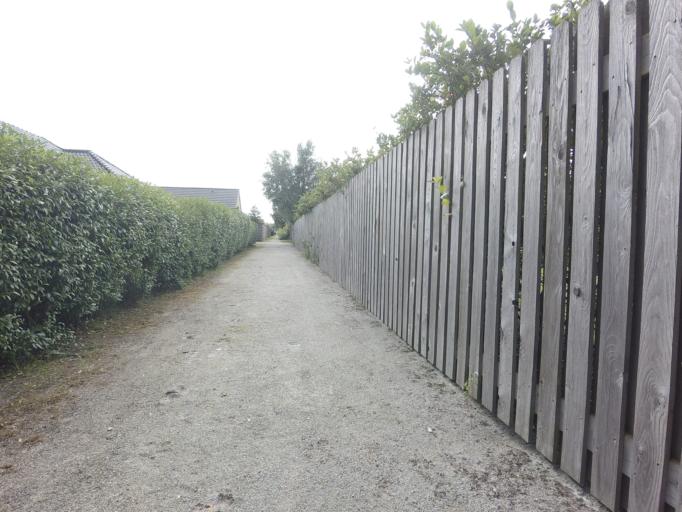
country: DK
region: North Denmark
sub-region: Jammerbugt Kommune
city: Pandrup
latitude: 57.3646
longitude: 9.7216
